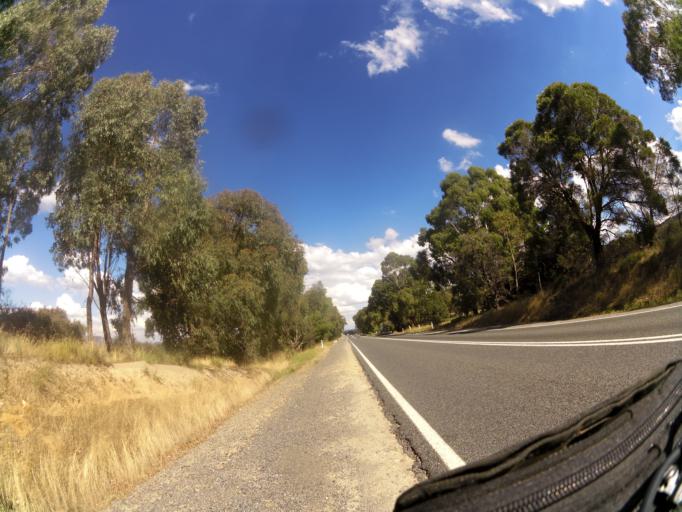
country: AU
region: Victoria
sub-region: Mansfield
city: Mansfield
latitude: -36.8869
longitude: 145.9951
